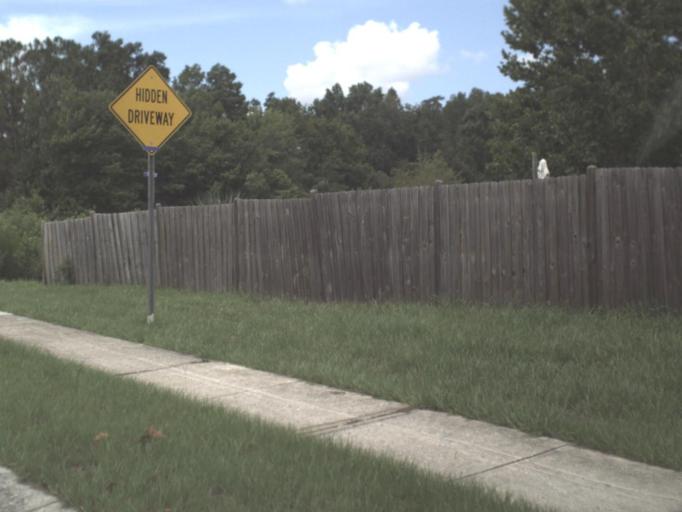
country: US
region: Florida
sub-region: Pasco County
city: Elfers
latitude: 28.2107
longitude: -82.6934
